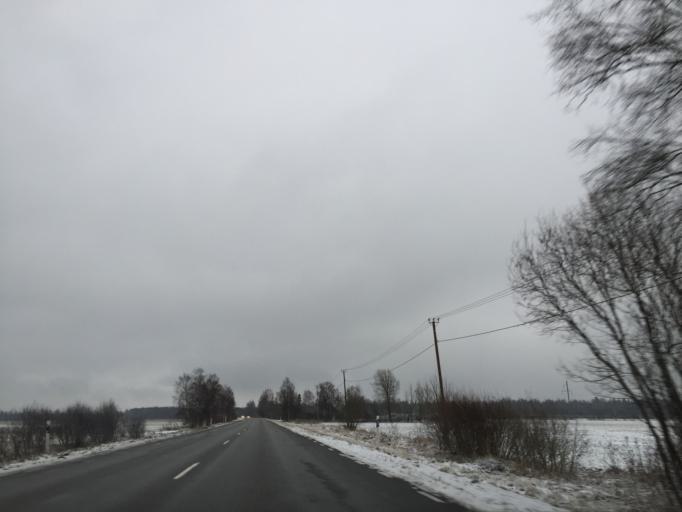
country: EE
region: Laeaene
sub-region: Lihula vald
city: Lihula
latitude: 58.6379
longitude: 23.8603
